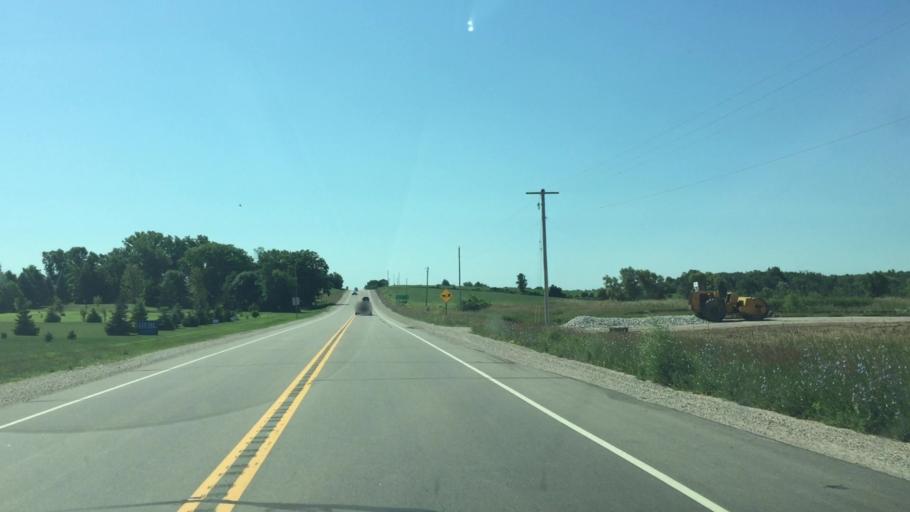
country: US
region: Wisconsin
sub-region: Calumet County
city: Chilton
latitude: 44.0168
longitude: -88.1496
